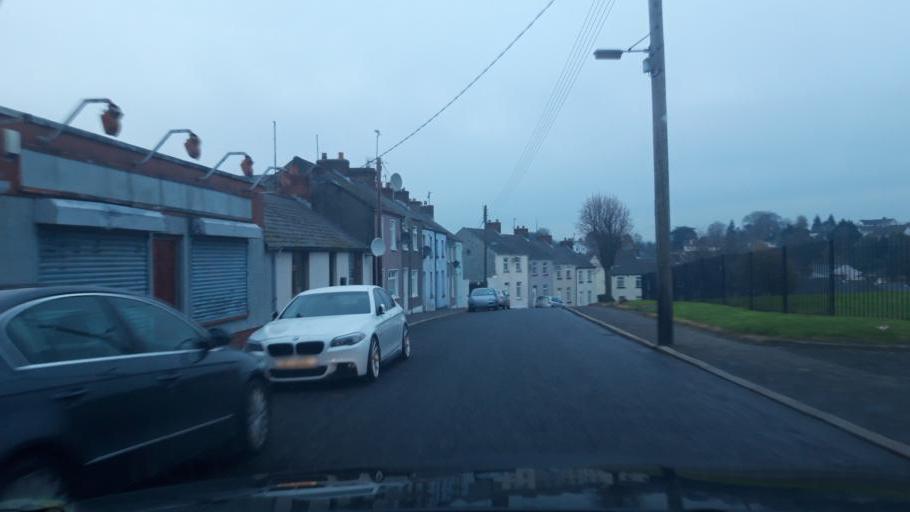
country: GB
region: Northern Ireland
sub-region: Newry and Mourne District
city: Newry
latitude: 54.1780
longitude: -6.3321
